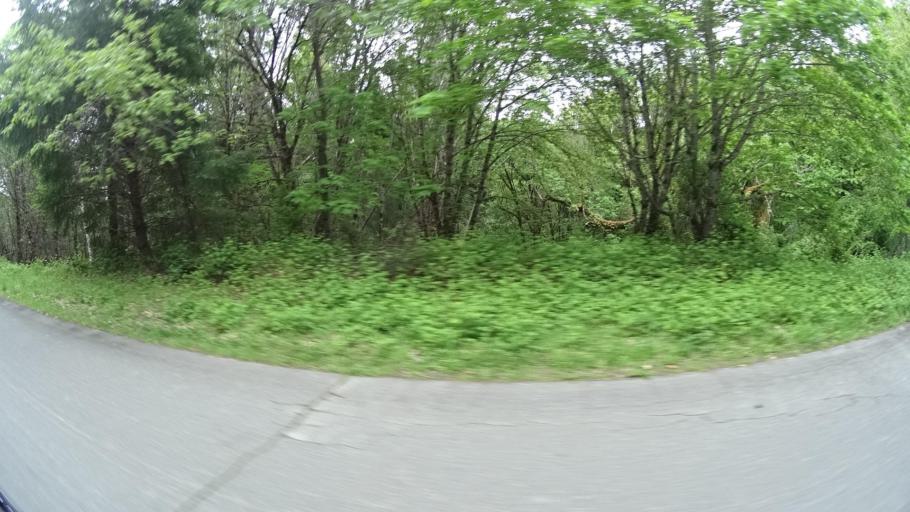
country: US
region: California
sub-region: Humboldt County
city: Willow Creek
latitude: 41.1176
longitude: -123.7213
